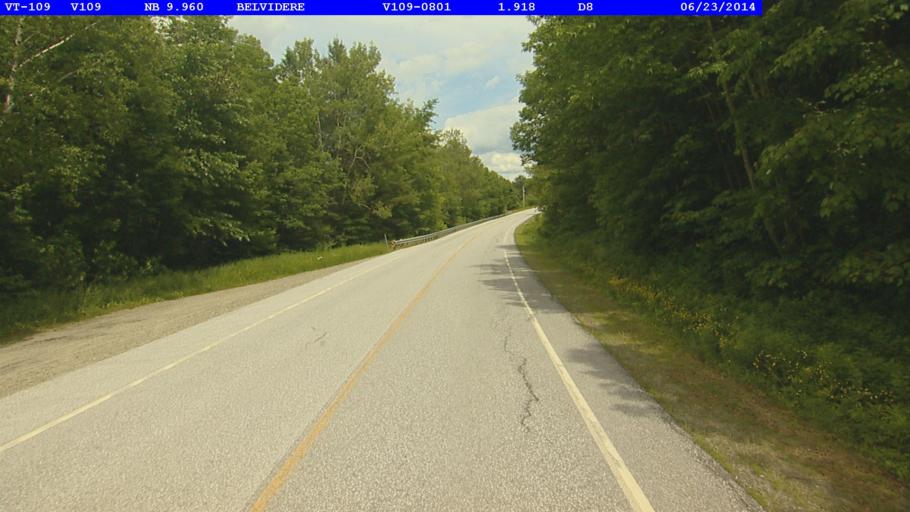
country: US
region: Vermont
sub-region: Lamoille County
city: Johnson
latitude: 44.7465
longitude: -72.7087
